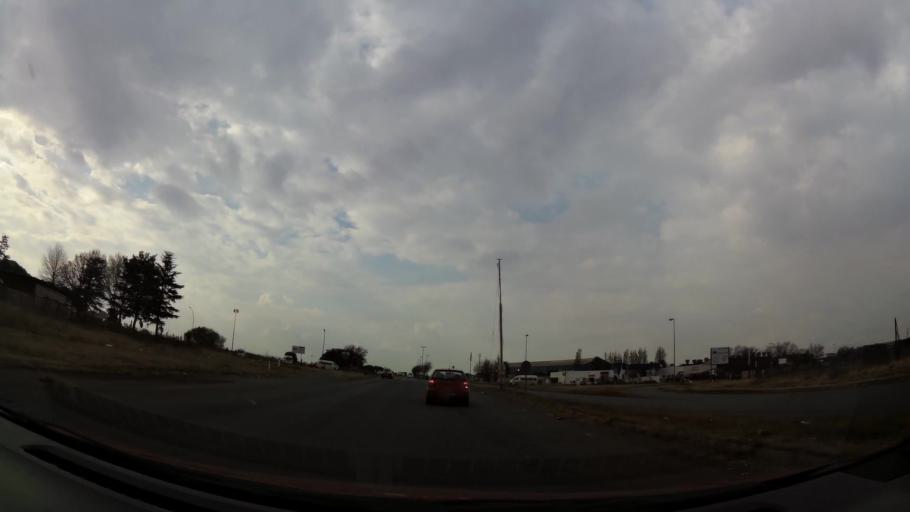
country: ZA
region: Gauteng
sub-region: Sedibeng District Municipality
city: Vanderbijlpark
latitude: -26.6604
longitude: 27.8454
